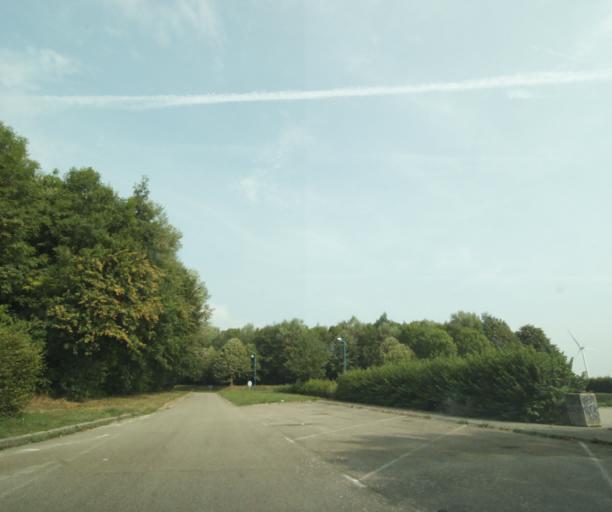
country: FR
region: Lower Normandy
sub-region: Departement du Calvados
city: Falaise
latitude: 48.9367
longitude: -0.2082
